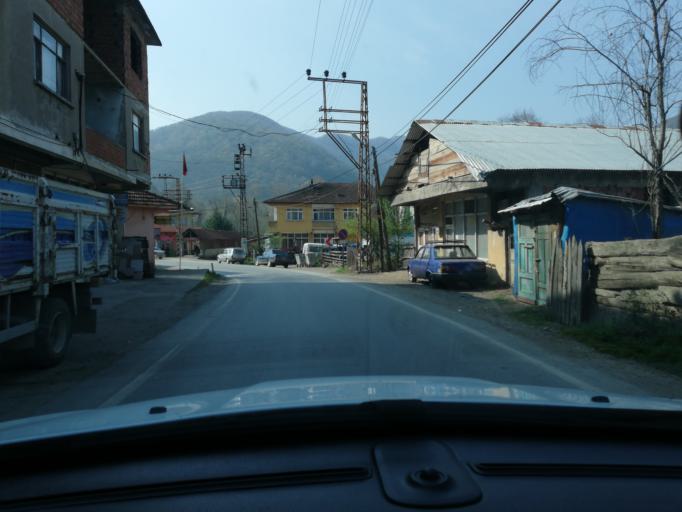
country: TR
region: Karabuk
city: Yenice
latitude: 41.2140
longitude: 32.3625
